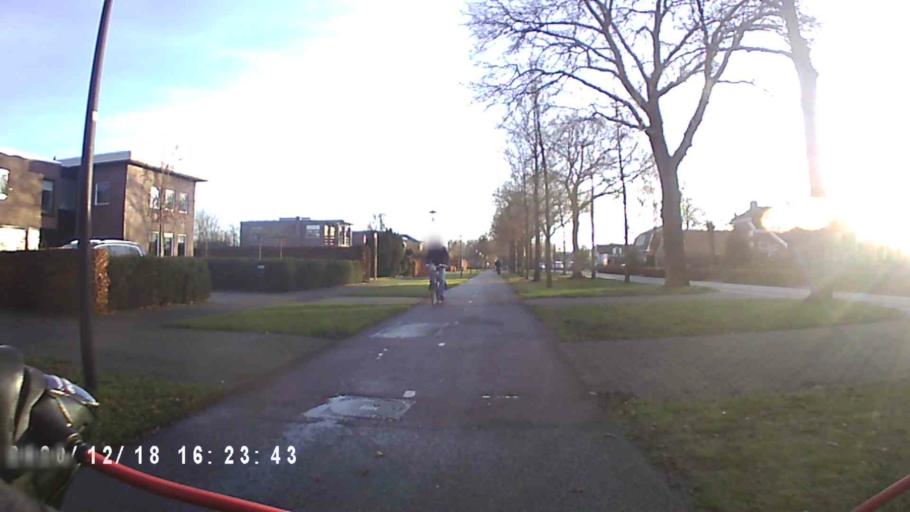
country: NL
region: Drenthe
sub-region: Gemeente Tynaarlo
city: Zuidlaren
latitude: 53.0887
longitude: 6.6926
